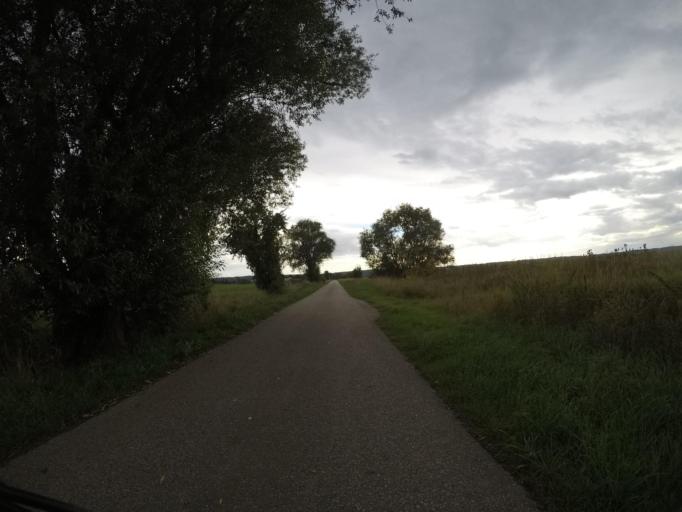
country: DE
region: Lower Saxony
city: Neu Darchau
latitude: 53.2558
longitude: 10.8757
